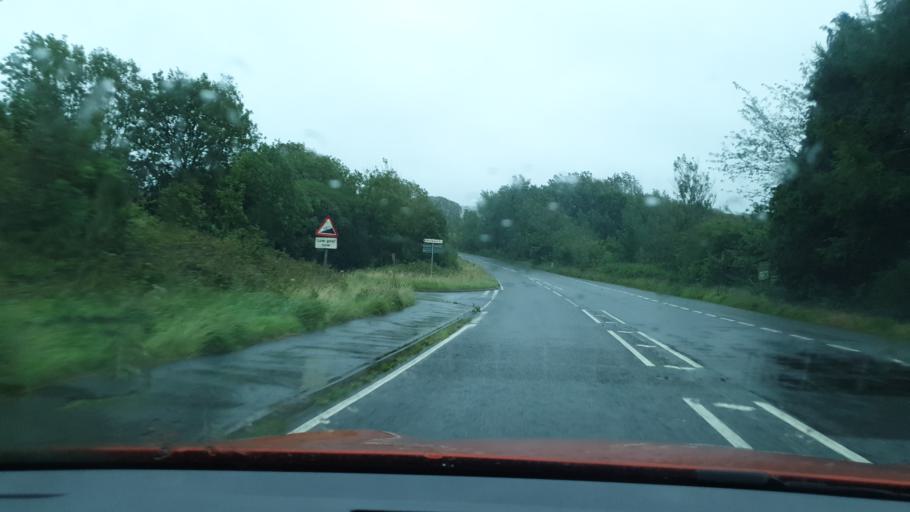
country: GB
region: England
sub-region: Cumbria
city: Askam in Furness
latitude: 54.2560
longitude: -3.1704
